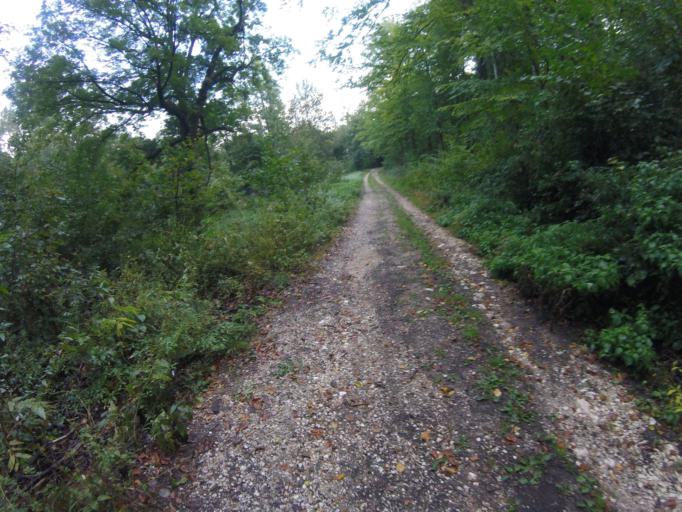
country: HU
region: Pest
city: Pilisszentkereszt
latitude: 47.7031
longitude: 18.8795
